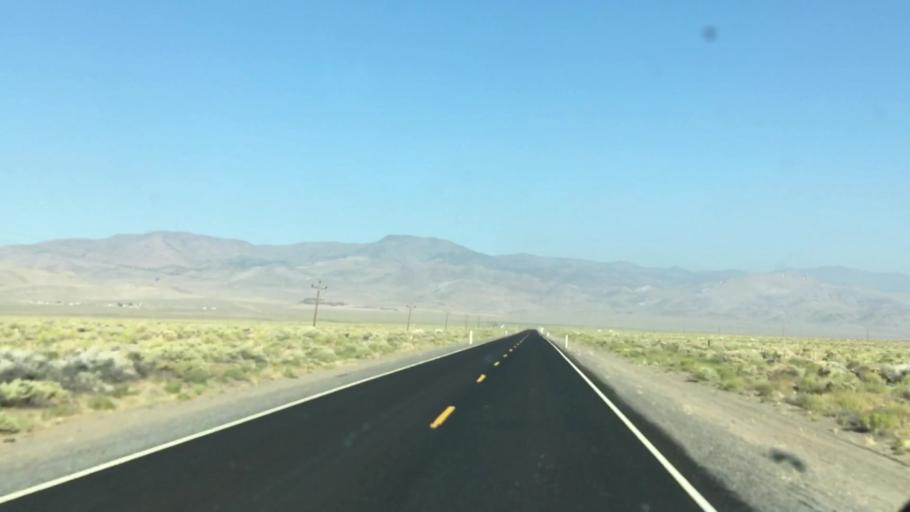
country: US
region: Nevada
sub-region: Lyon County
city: Fernley
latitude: 39.6460
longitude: -119.3124
